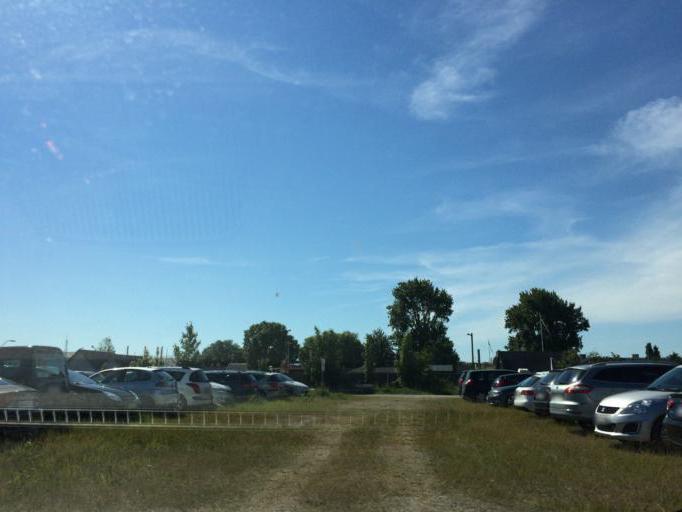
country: DK
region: Capital Region
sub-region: Dragor Kommune
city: Dragor
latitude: 55.6354
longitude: 12.6539
